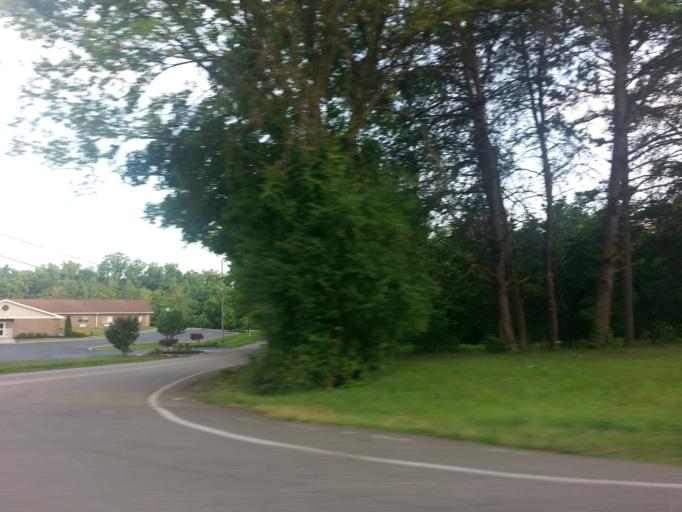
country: US
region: Tennessee
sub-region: Knox County
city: Knoxville
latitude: 35.9846
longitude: -83.8609
